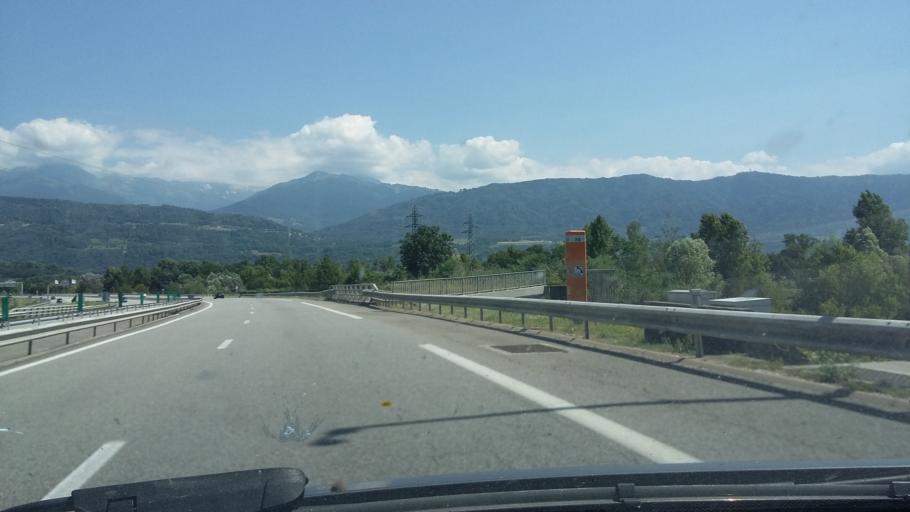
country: FR
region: Rhone-Alpes
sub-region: Departement de la Savoie
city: Les Marches
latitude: 45.4846
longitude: 6.0246
